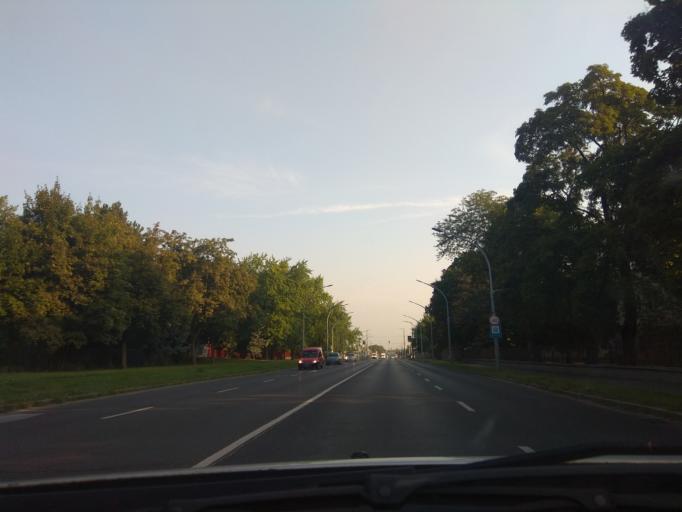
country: HU
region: Borsod-Abauj-Zemplen
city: Miskolc
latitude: 48.1240
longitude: 20.7860
